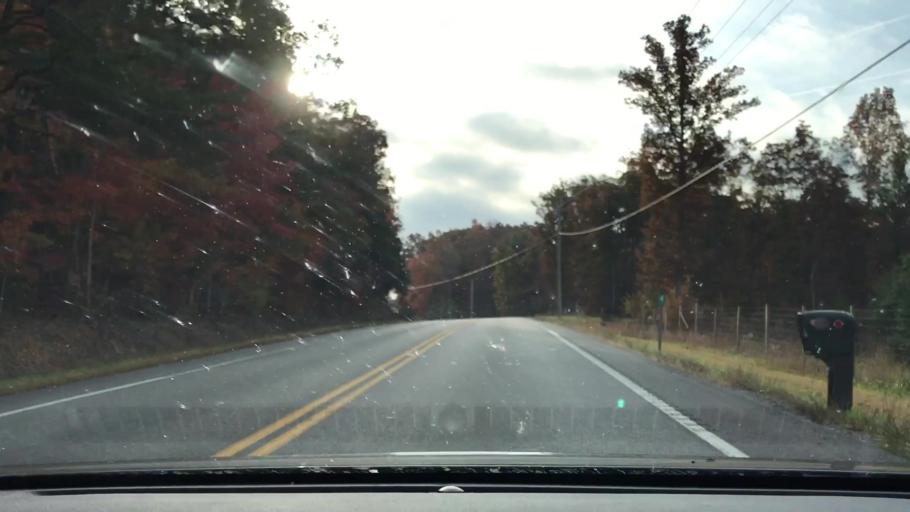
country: US
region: Tennessee
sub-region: Putnam County
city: Monterey
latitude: 36.1296
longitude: -85.2046
